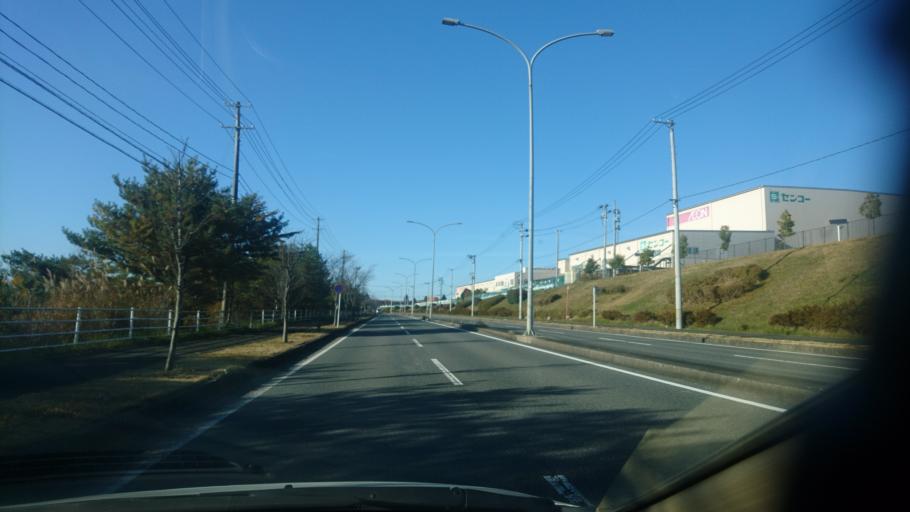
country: JP
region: Miyagi
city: Tomiya
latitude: 38.4558
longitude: 140.9308
